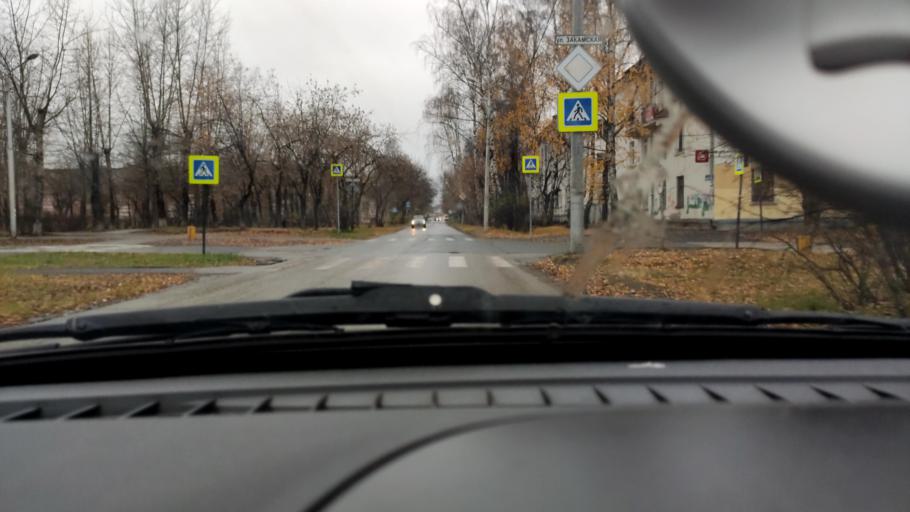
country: RU
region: Perm
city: Kultayevo
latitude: 57.9969
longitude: 55.9447
